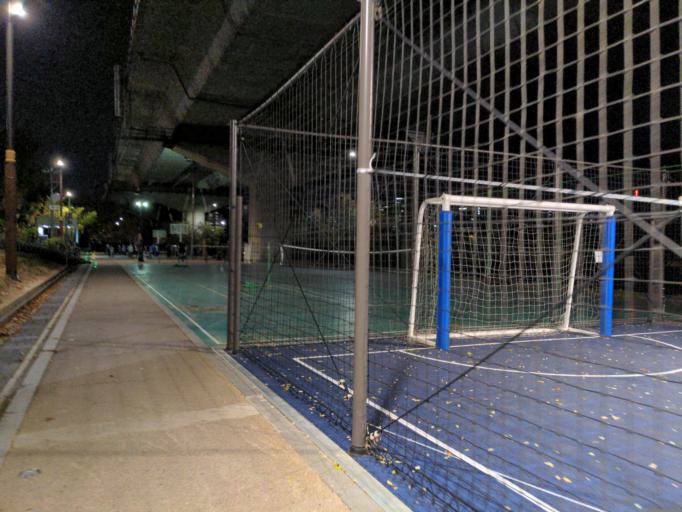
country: KR
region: Seoul
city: Seoul
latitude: 37.5623
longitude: 127.0492
